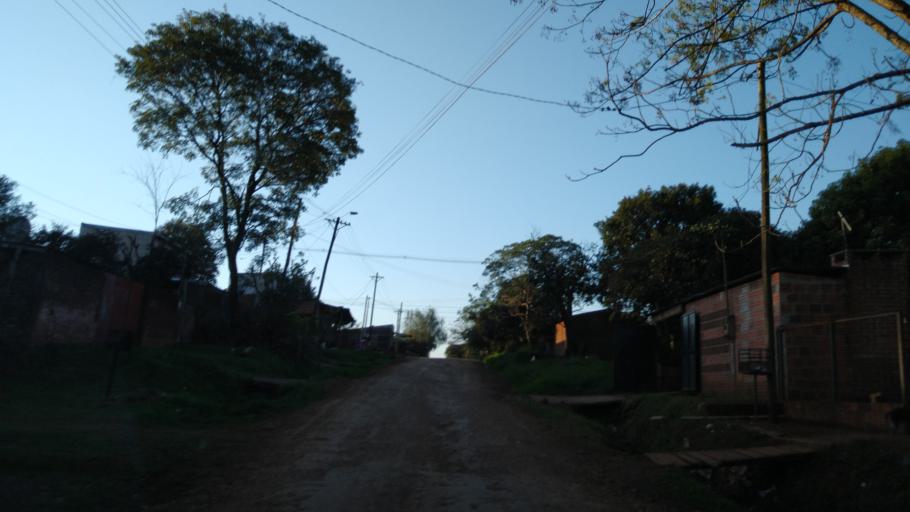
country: AR
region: Misiones
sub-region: Departamento de Capital
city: Posadas
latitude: -27.4206
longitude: -55.9204
